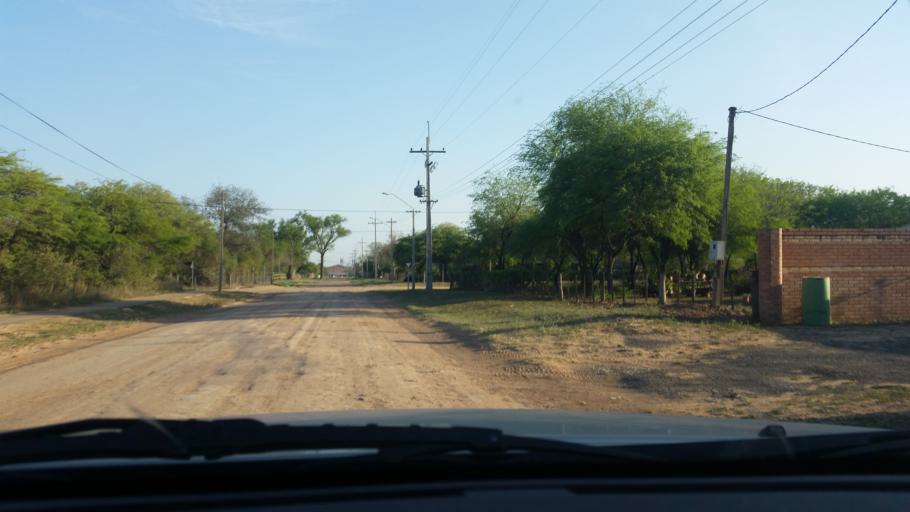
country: PY
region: Boqueron
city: Filadelfia
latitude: -22.3457
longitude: -60.0388
